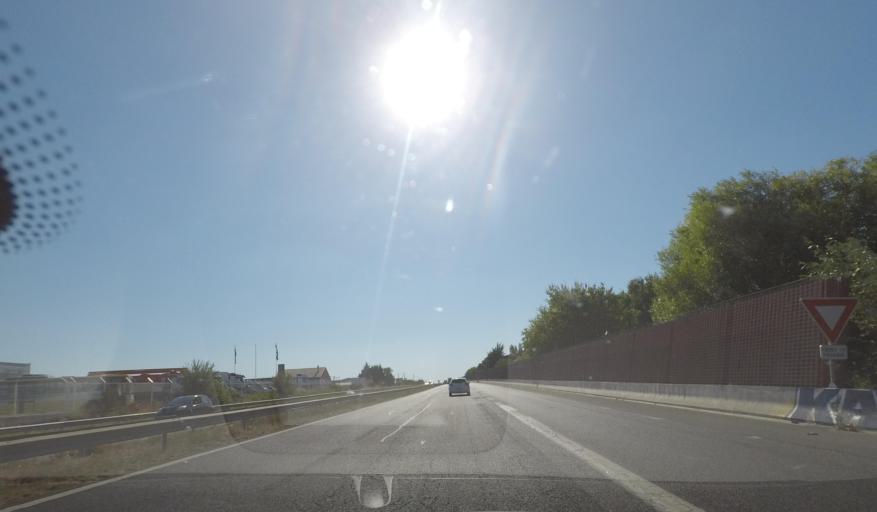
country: FR
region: Pays de la Loire
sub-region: Departement de la Loire-Atlantique
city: Montoir-de-Bretagne
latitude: 47.3278
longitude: -2.1336
